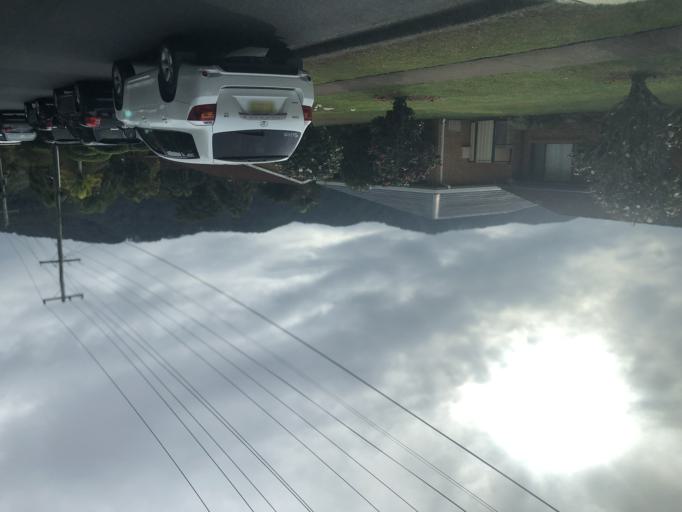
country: AU
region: New South Wales
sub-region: Coffs Harbour
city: Coffs Harbour
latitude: -30.2845
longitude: 153.1114
